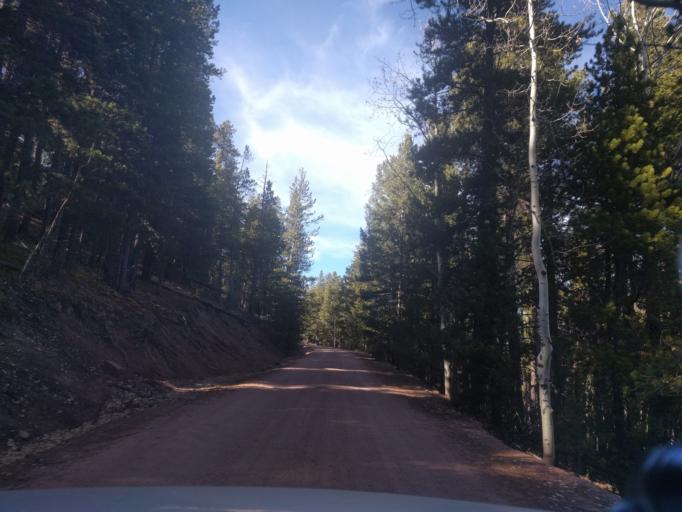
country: US
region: Colorado
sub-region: Douglas County
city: Perry Park
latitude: 39.2043
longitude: -105.0518
